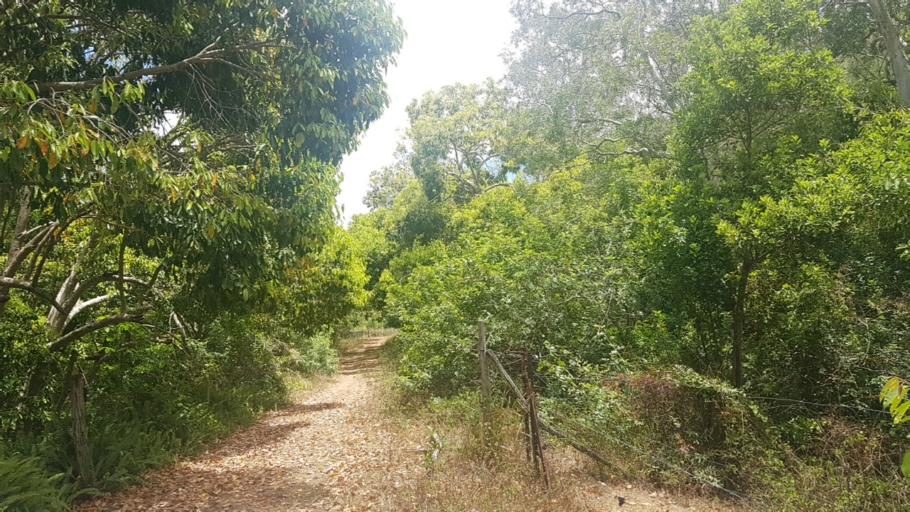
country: NC
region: South Province
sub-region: Dumbea
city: Dumbea
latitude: -22.1719
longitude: 166.4692
